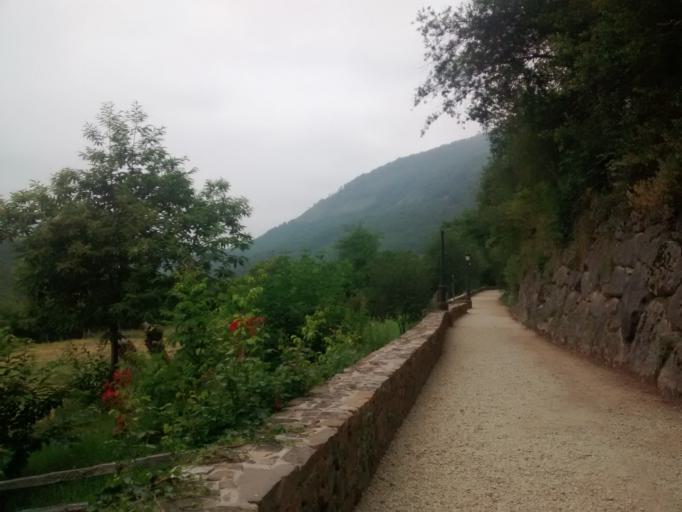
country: ES
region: Cantabria
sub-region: Provincia de Cantabria
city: Pesquera
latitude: 43.1451
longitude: -4.1939
